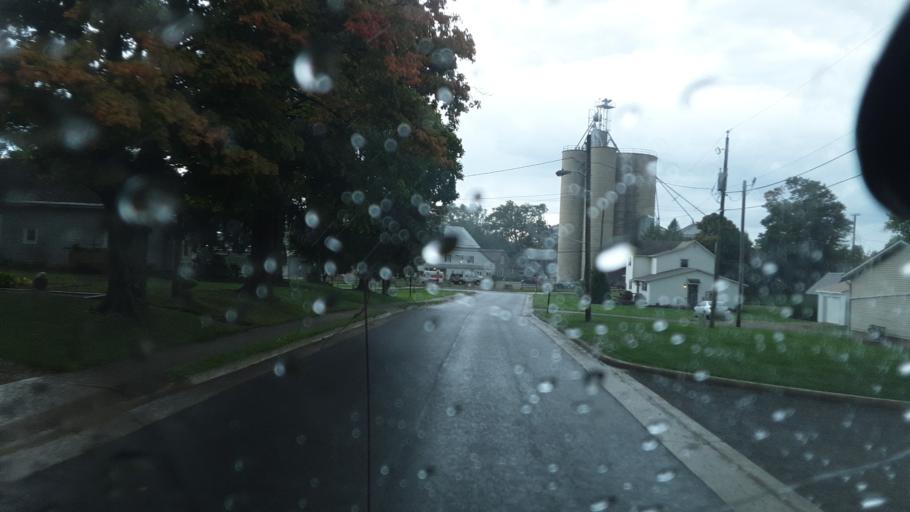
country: US
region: Ohio
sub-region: Knox County
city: Centerburg
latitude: 40.3075
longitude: -82.6981
